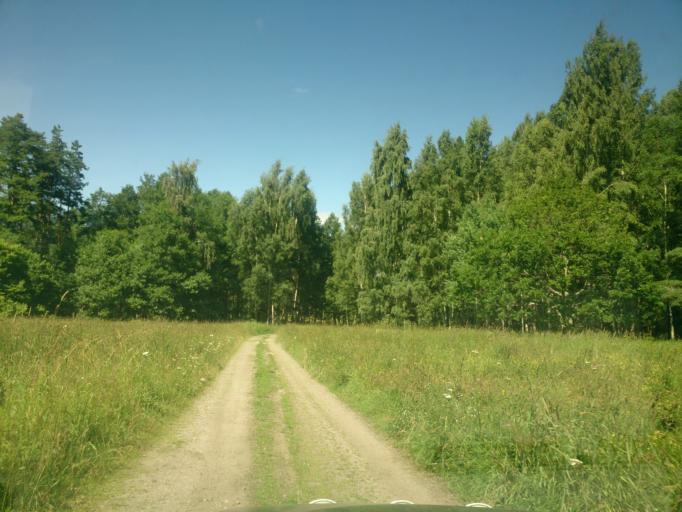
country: SE
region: OEstergoetland
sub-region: Atvidabergs Kommun
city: Atvidaberg
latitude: 58.2420
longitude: 15.9665
